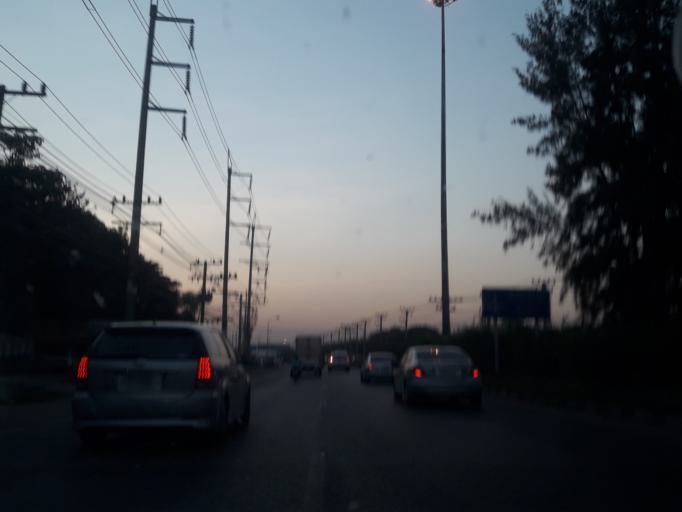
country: TH
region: Pathum Thani
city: Thanyaburi
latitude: 14.0670
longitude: 100.7033
